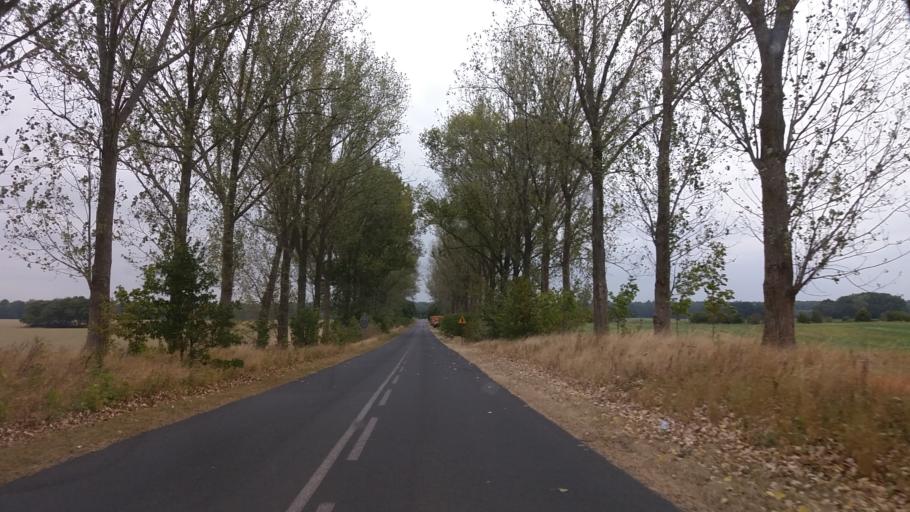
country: PL
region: West Pomeranian Voivodeship
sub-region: Powiat choszczenski
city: Krzecin
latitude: 52.9812
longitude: 15.5046
